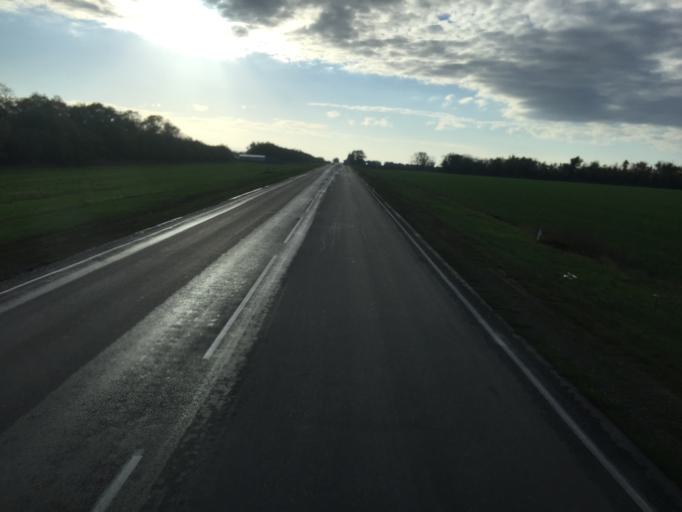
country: RU
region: Rostov
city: Kagal'nitskaya
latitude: 46.8513
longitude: 40.2026
